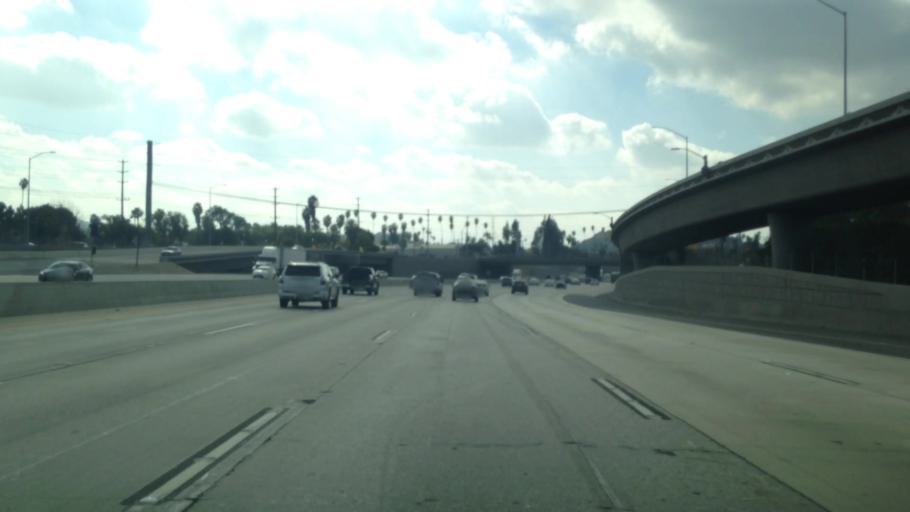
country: US
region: California
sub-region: Riverside County
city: Riverside
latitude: 33.9767
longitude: -117.3719
